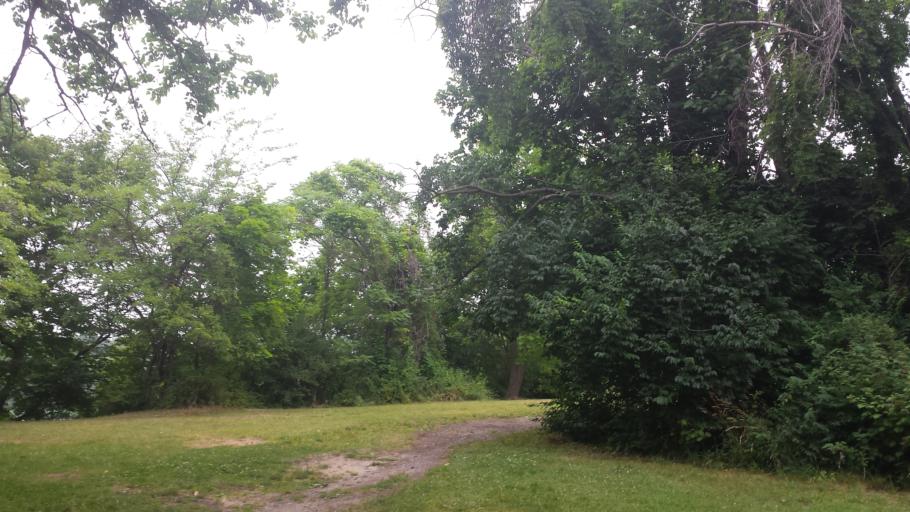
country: US
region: New York
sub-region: Westchester County
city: Crugers
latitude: 41.2344
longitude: -73.9439
